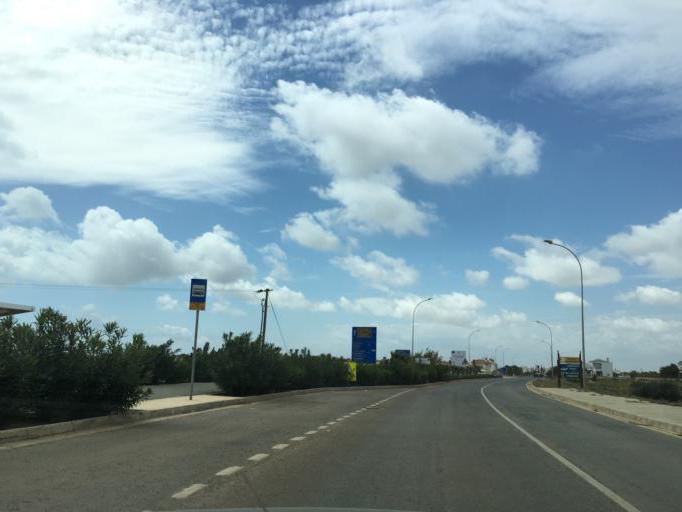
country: CY
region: Ammochostos
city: Liopetri
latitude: 34.9809
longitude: 33.9341
